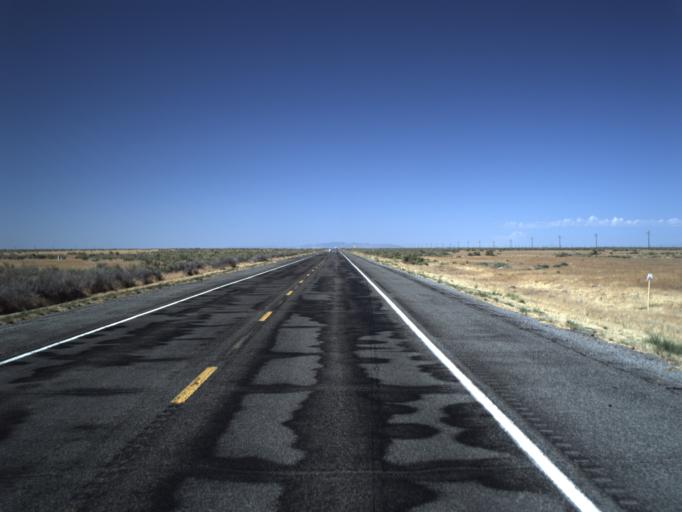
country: US
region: Utah
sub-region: Millard County
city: Delta
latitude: 39.4552
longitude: -112.4402
